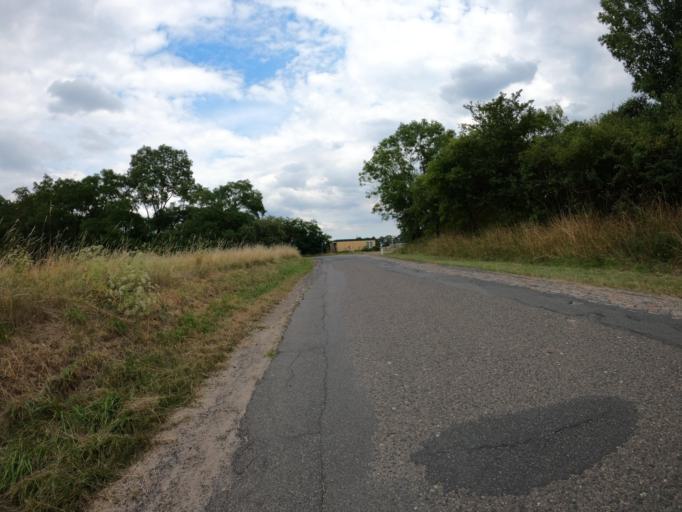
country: DE
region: Mecklenburg-Vorpommern
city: Woldegk
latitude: 53.3548
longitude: 13.5932
